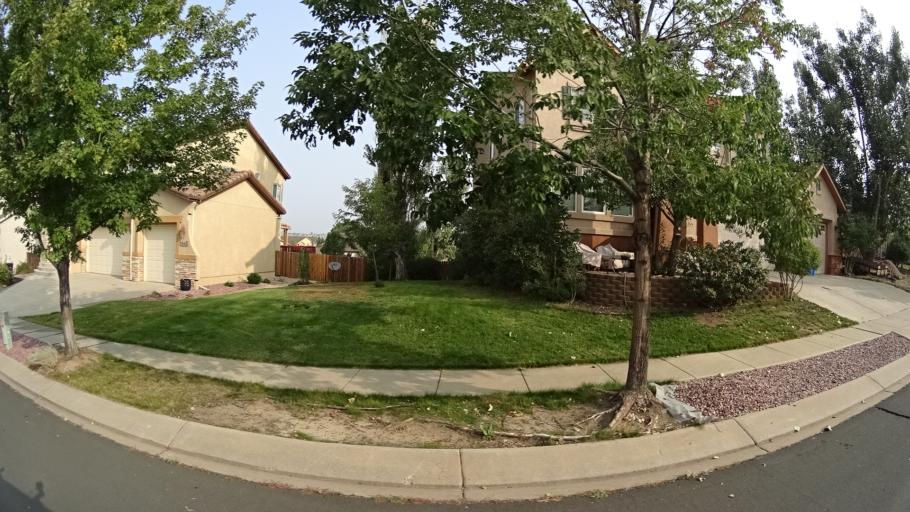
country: US
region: Colorado
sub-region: El Paso County
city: Cimarron Hills
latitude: 38.9322
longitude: -104.7353
